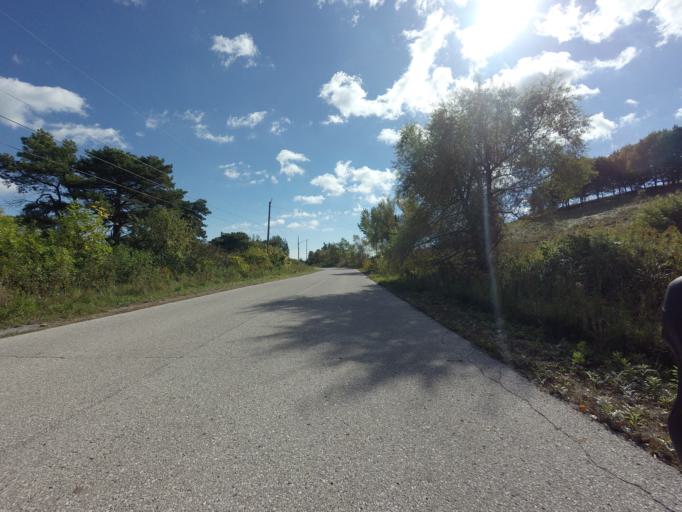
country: CA
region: Ontario
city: Ajax
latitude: 43.8149
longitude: -79.0546
